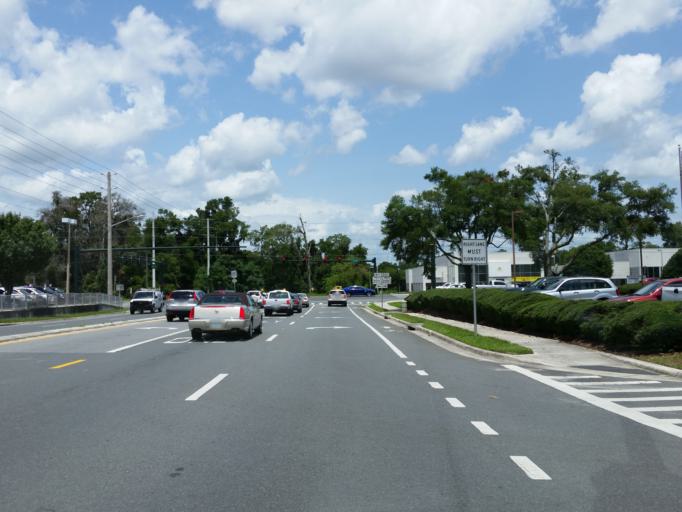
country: US
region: Florida
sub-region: Marion County
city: Ocala
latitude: 29.1443
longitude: -82.1896
